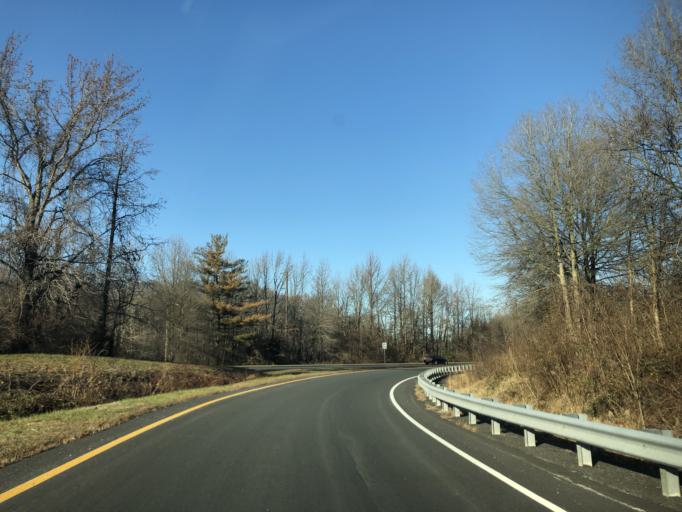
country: US
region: New Jersey
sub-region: Salem County
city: Carneys Point
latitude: 39.7096
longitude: -75.4431
